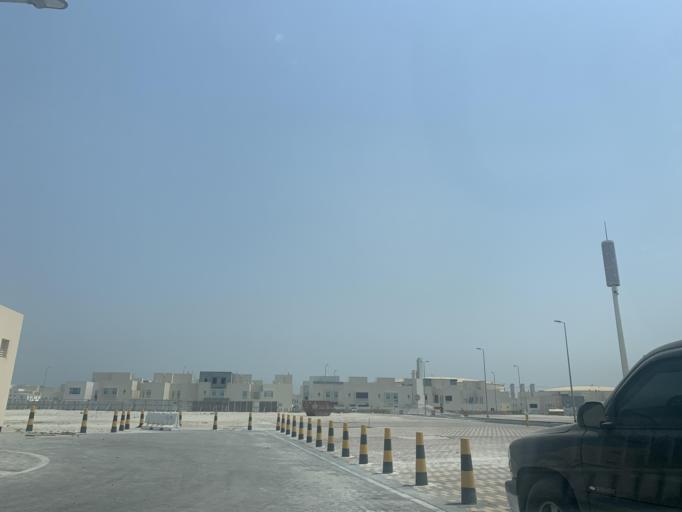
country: BH
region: Muharraq
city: Al Hadd
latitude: 26.2341
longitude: 50.6636
